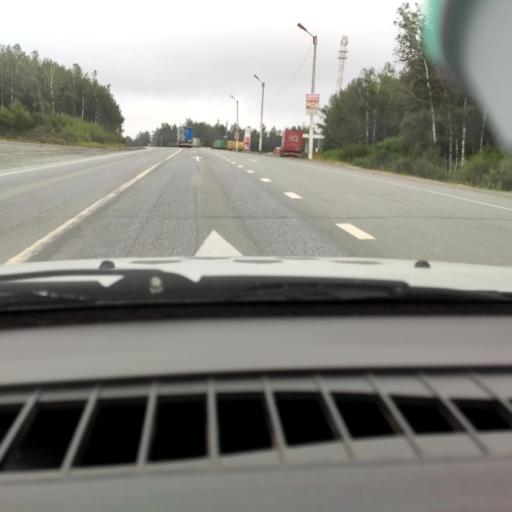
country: RU
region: Chelyabinsk
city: Zlatoust
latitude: 55.0196
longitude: 59.7317
